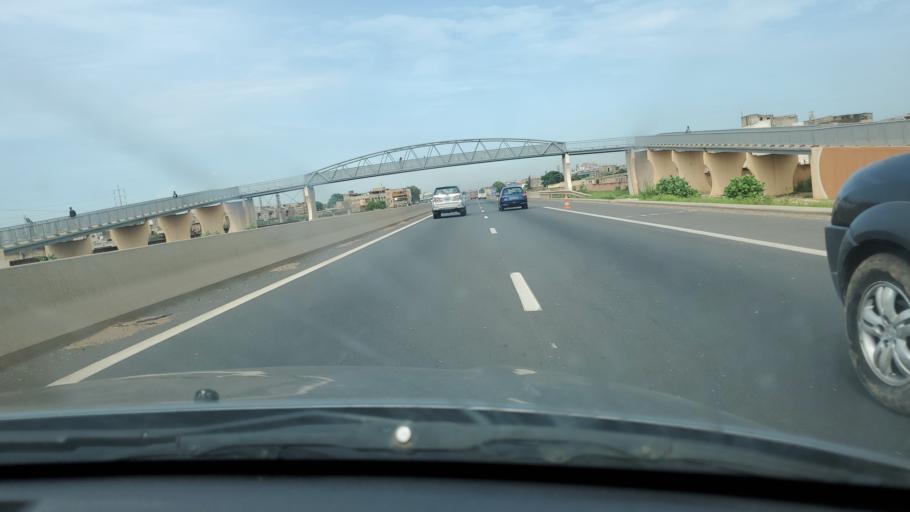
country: SN
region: Dakar
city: Pikine
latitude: 14.7564
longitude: -17.3607
